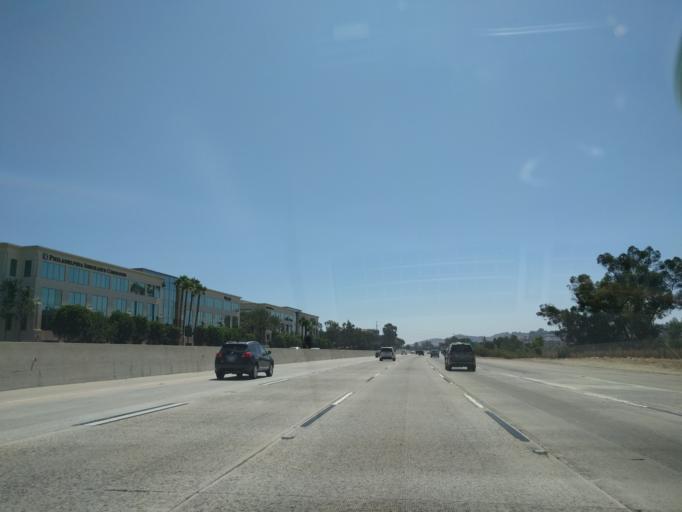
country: US
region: California
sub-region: Orange County
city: Mission Viejo
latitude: 33.5693
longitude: -117.6721
